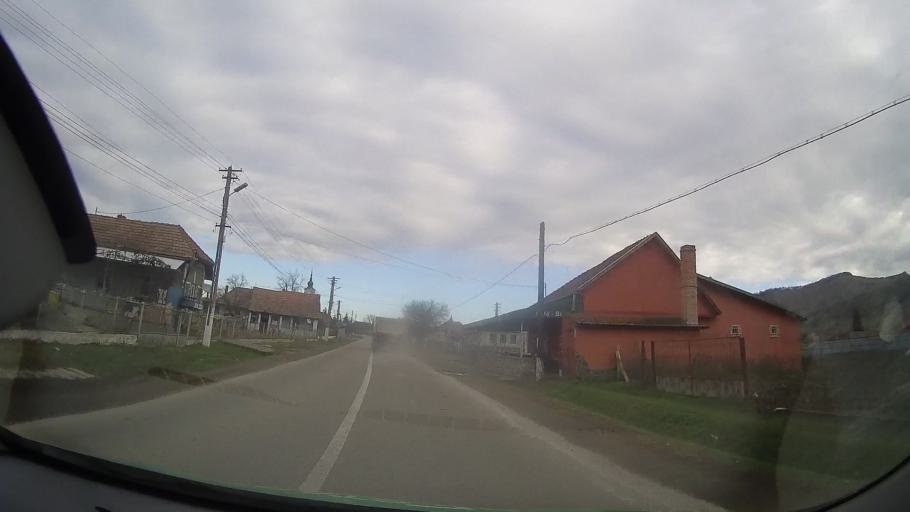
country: RO
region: Mures
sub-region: Comuna Iernut
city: Iernut
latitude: 46.4724
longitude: 24.2249
